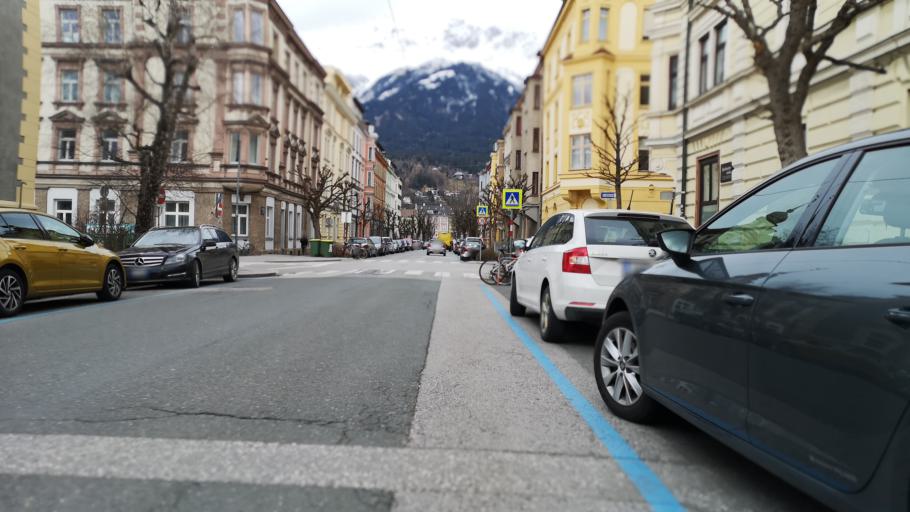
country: AT
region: Tyrol
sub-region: Innsbruck Stadt
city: Innsbruck
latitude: 47.2609
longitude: 11.3897
